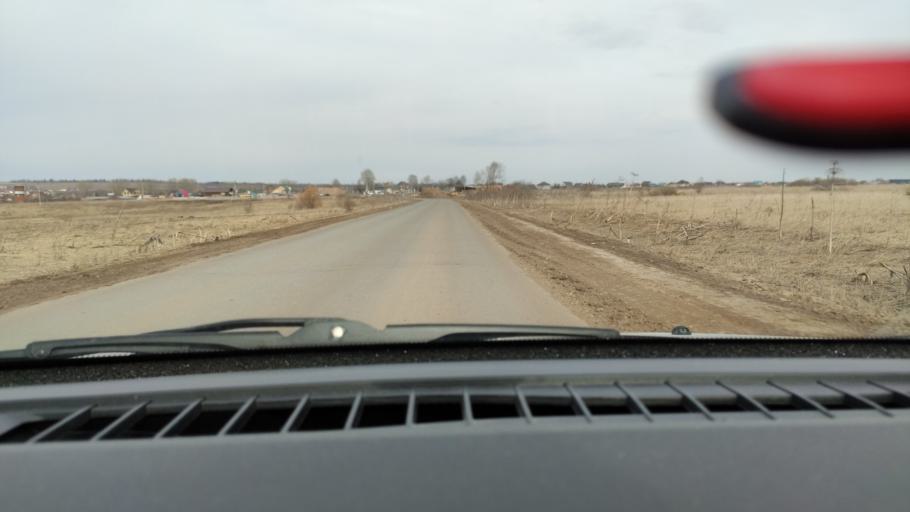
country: RU
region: Perm
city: Kultayevo
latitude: 57.9037
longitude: 55.9920
